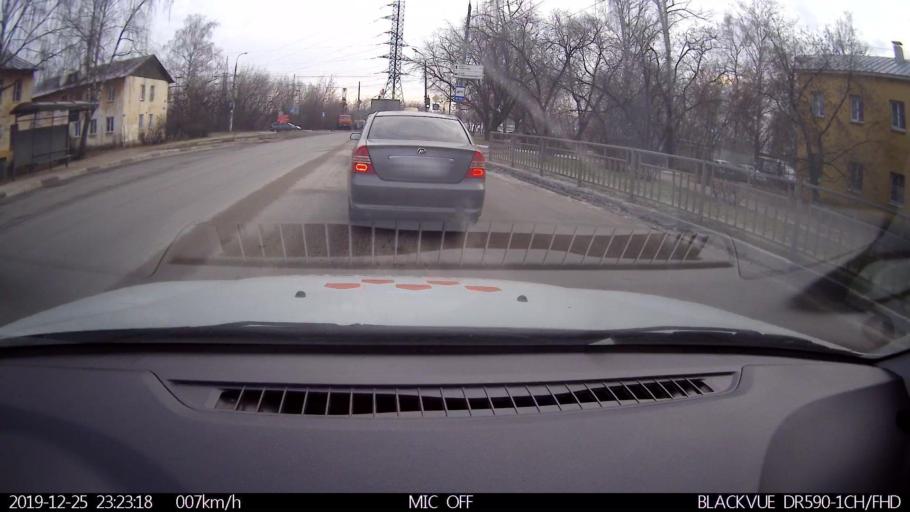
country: RU
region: Nizjnij Novgorod
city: Gorbatovka
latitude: 56.3512
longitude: 43.8352
